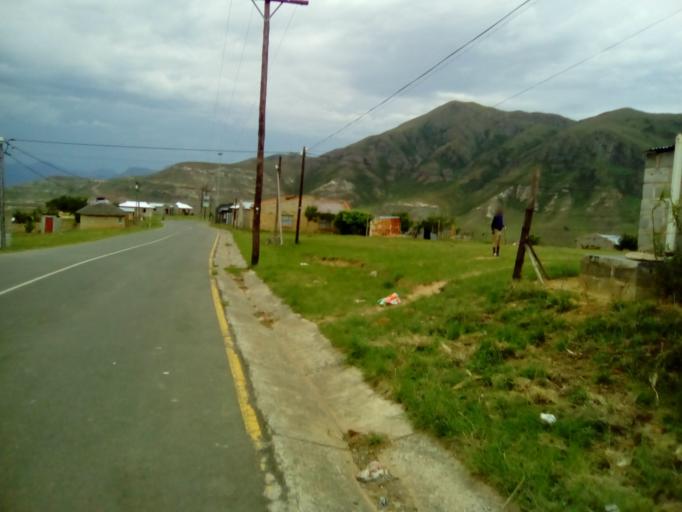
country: LS
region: Qacha's Nek
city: Qacha's Nek
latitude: -30.1068
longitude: 28.6810
